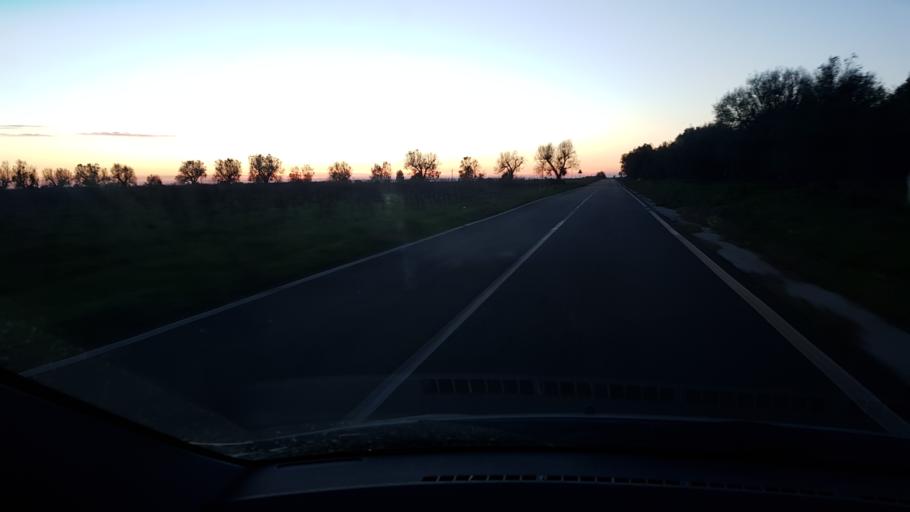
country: IT
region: Apulia
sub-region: Provincia di Brindisi
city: Tuturano
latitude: 40.5273
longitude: 17.9098
